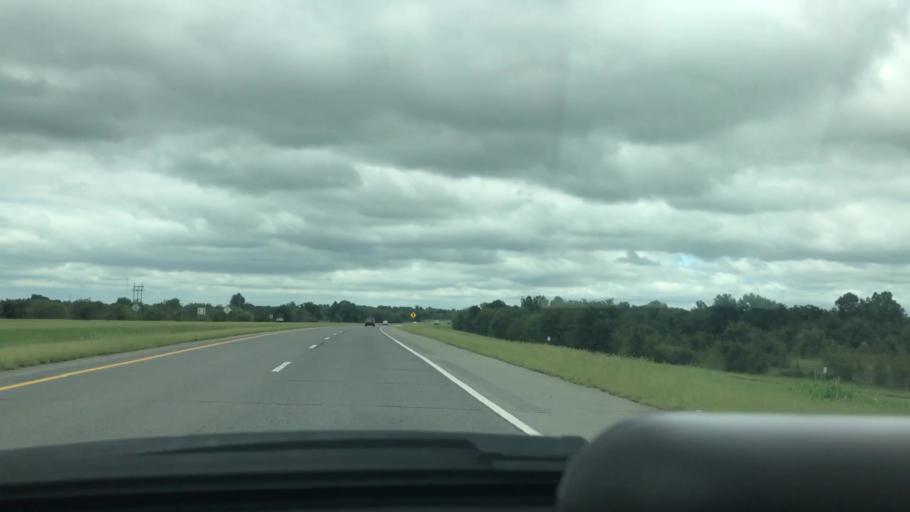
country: US
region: Oklahoma
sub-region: McIntosh County
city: Checotah
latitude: 35.5767
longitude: -95.4911
